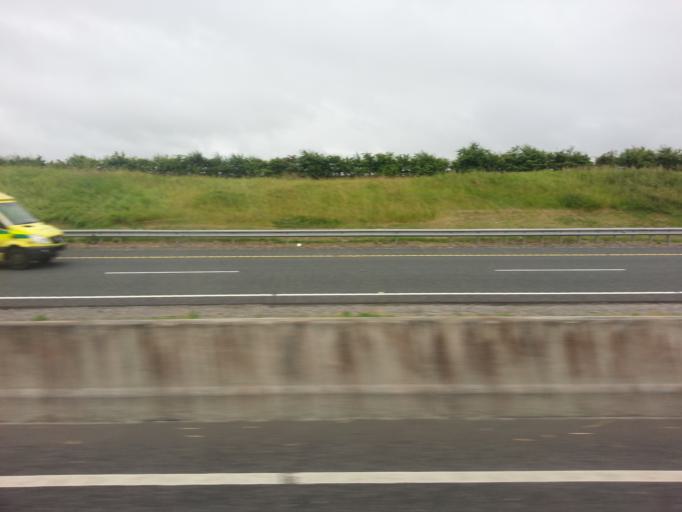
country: IE
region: Leinster
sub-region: County Carlow
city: Carlow
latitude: 52.8041
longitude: -6.8632
